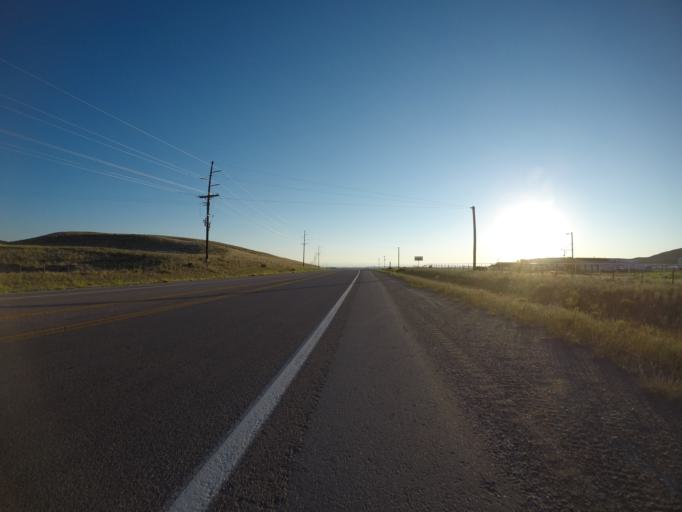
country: US
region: Wyoming
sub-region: Sublette County
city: Marbleton
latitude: 42.5666
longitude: -110.0991
